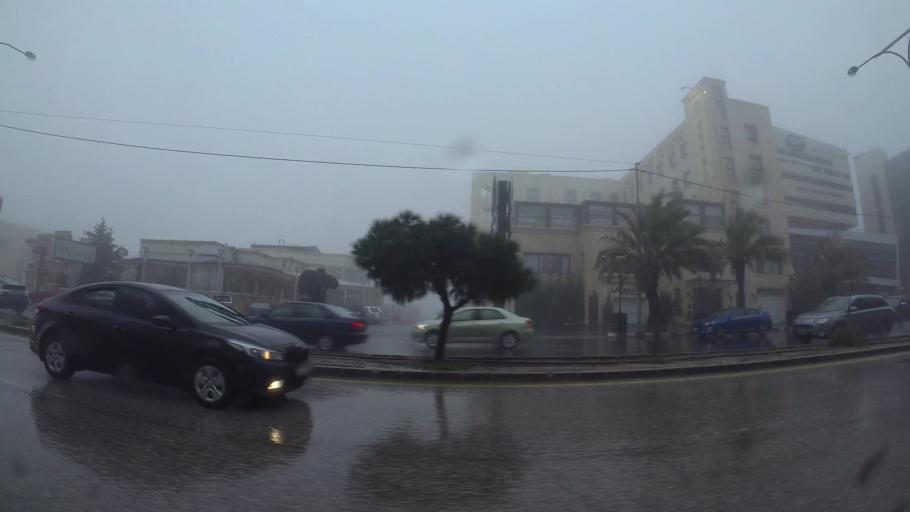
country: JO
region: Amman
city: Al Jubayhah
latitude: 31.9877
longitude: 35.8667
